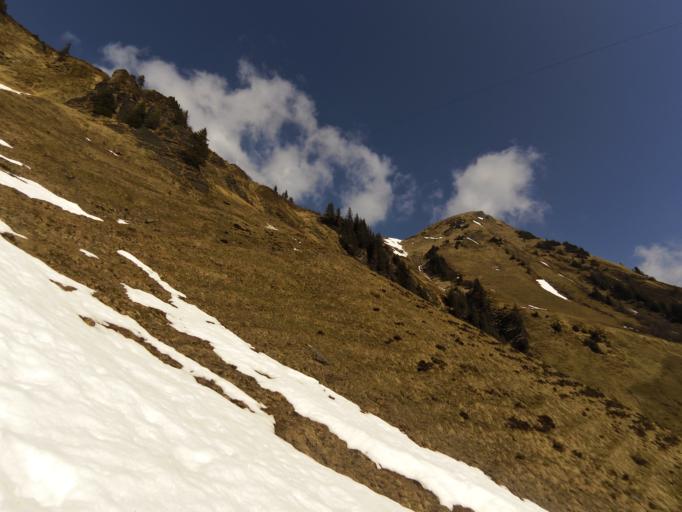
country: CH
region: Nidwalden
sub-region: Nidwalden
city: Emmetten
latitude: 46.9090
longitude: 8.4977
